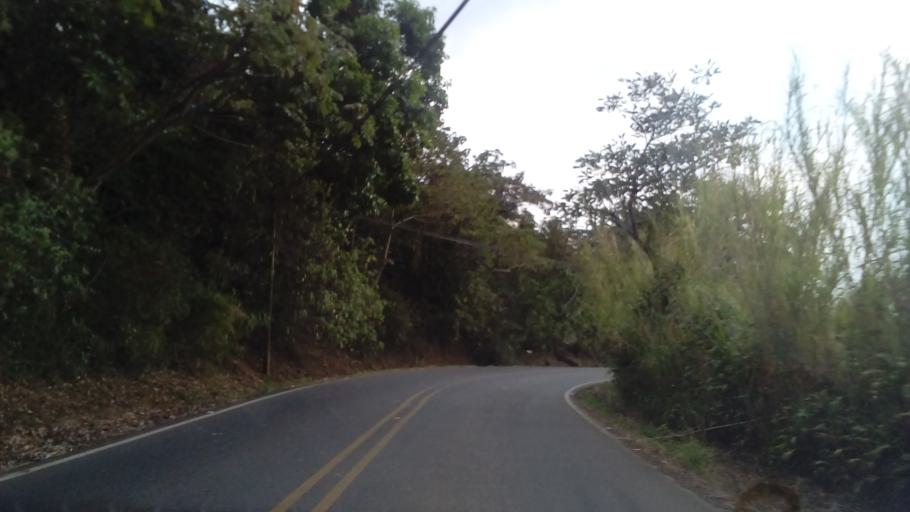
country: CR
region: Alajuela
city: Sabanilla
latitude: 10.0624
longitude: -84.2447
